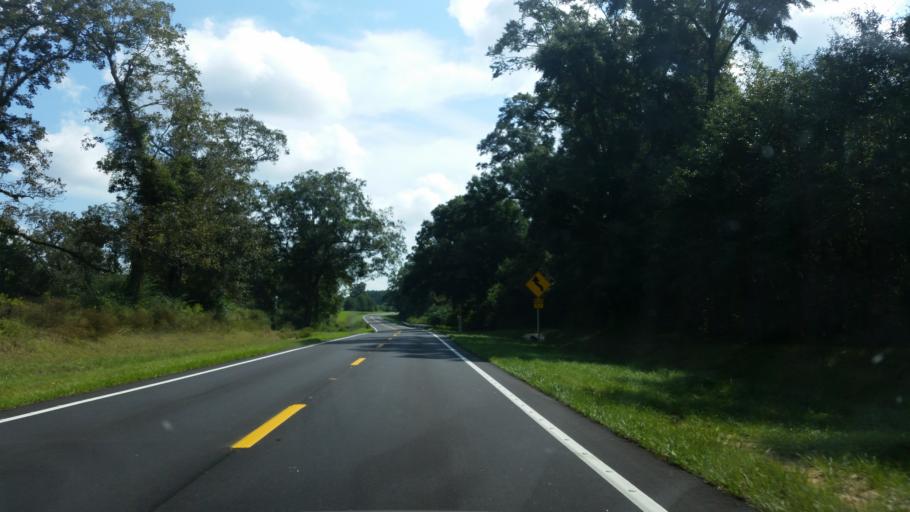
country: US
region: Florida
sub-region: Escambia County
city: Molino
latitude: 30.6970
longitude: -87.4184
